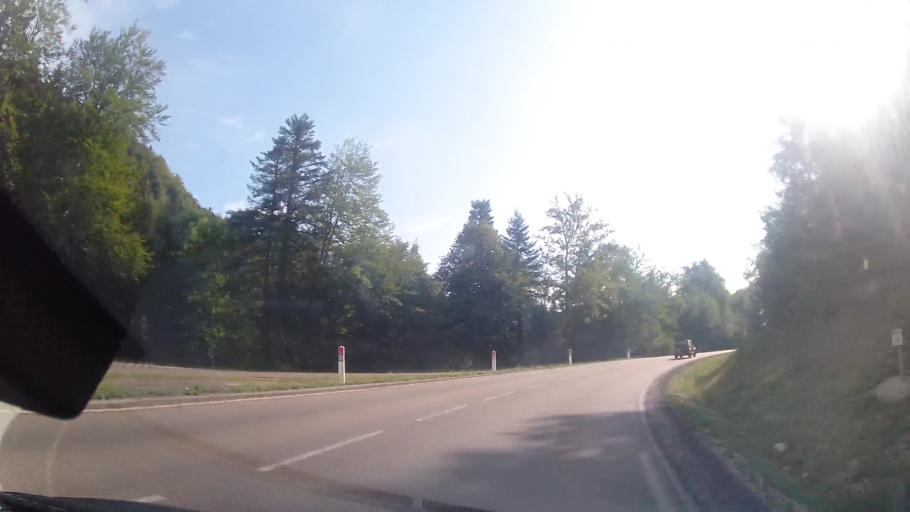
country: FR
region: Franche-Comte
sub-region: Departement du Jura
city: Clairvaux-les-Lacs
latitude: 46.6033
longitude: 5.8788
